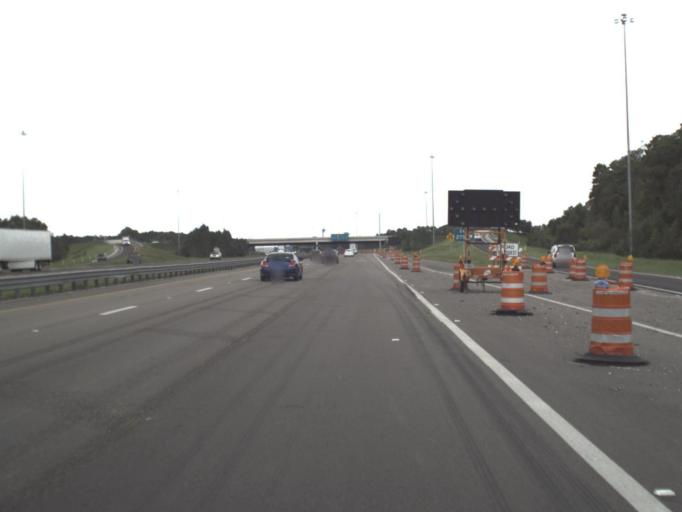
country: US
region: Florida
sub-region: Hillsborough County
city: Pebble Creek
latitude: 28.1998
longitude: -82.3813
